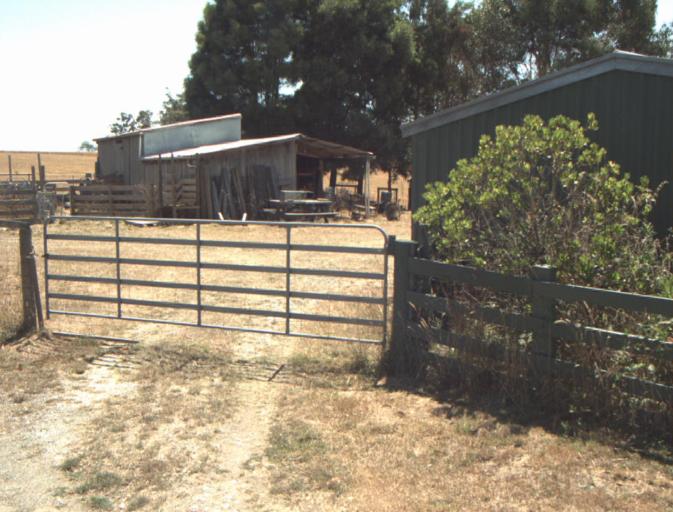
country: AU
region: Tasmania
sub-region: Launceston
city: Mayfield
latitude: -41.2451
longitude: 147.1317
